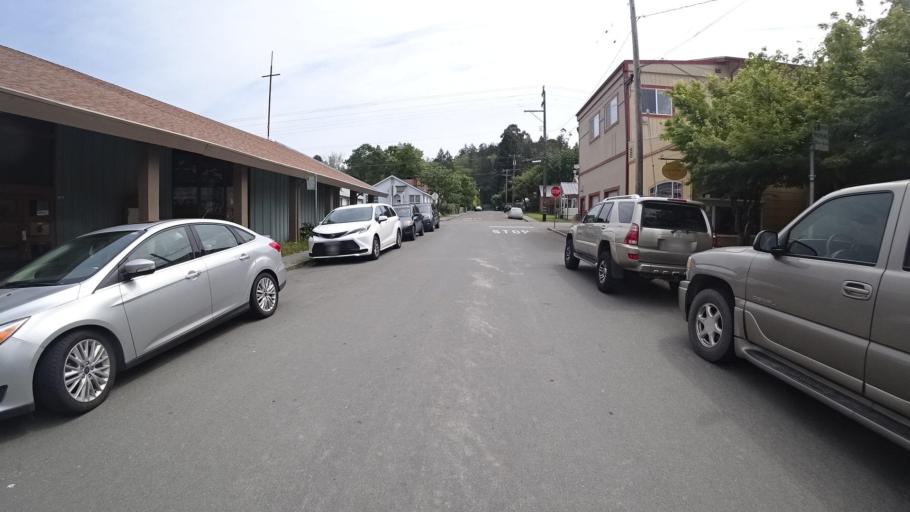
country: US
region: California
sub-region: Humboldt County
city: Redway
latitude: 40.1001
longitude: -123.7941
